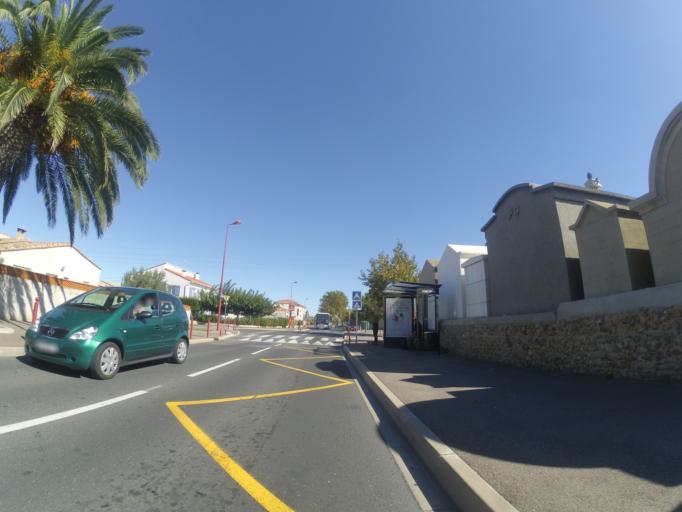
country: FR
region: Languedoc-Roussillon
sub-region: Departement des Pyrenees-Orientales
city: Saint-Esteve
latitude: 42.7095
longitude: 2.8499
